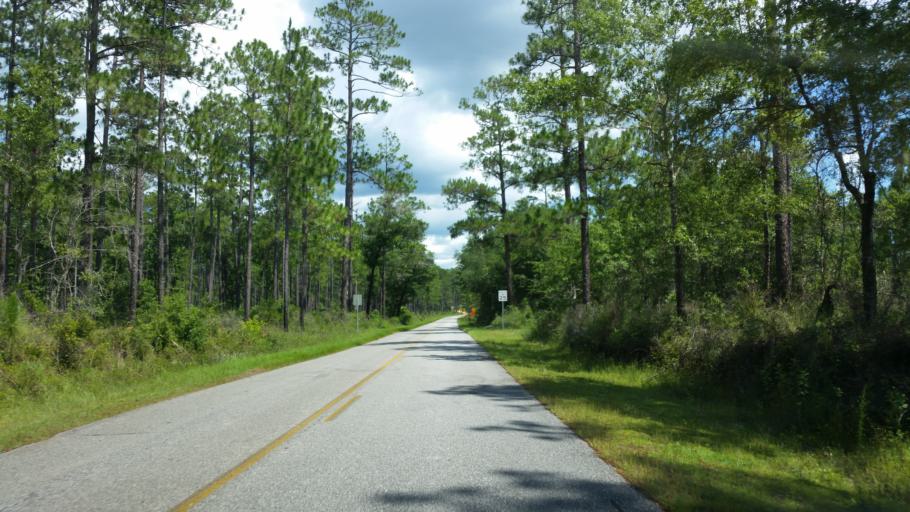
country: US
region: Florida
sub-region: Okaloosa County
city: Crestview
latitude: 30.7274
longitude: -86.7991
